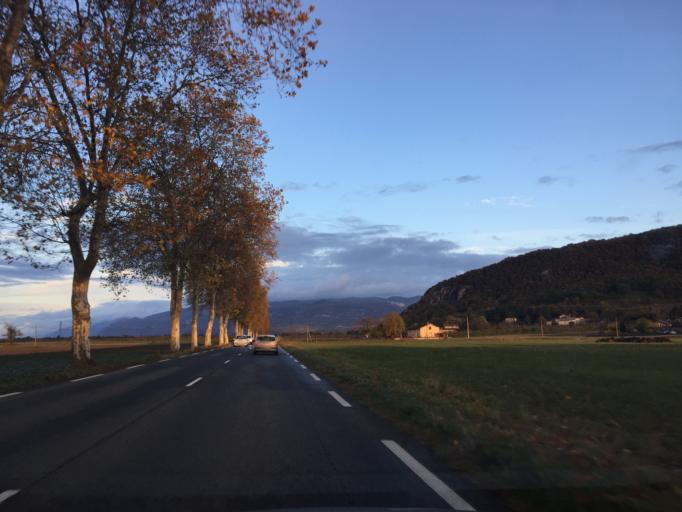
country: FR
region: Rhone-Alpes
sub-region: Departement de l'Isere
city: Saint-Lattier
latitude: 45.0630
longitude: 5.2187
